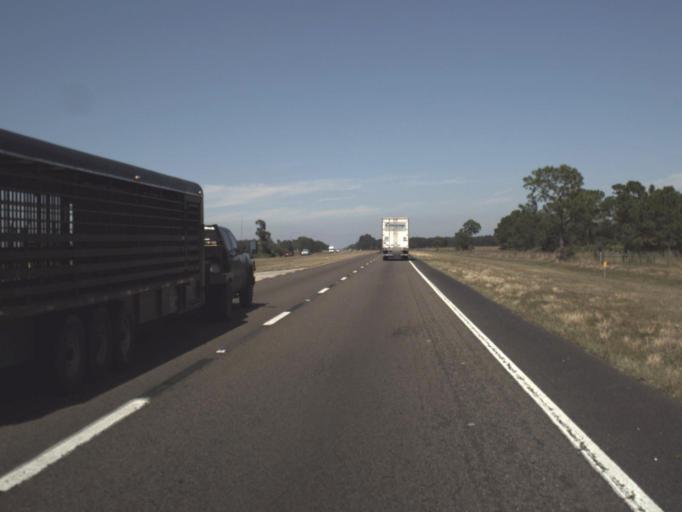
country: US
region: Florida
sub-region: Highlands County
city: Placid Lakes
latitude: 27.0734
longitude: -81.3358
